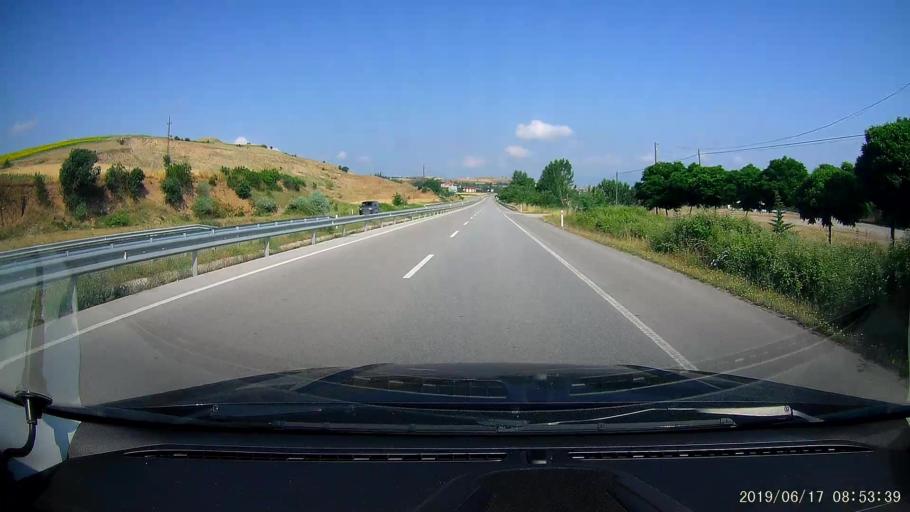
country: TR
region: Tokat
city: Erbaa
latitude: 40.7117
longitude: 36.4771
